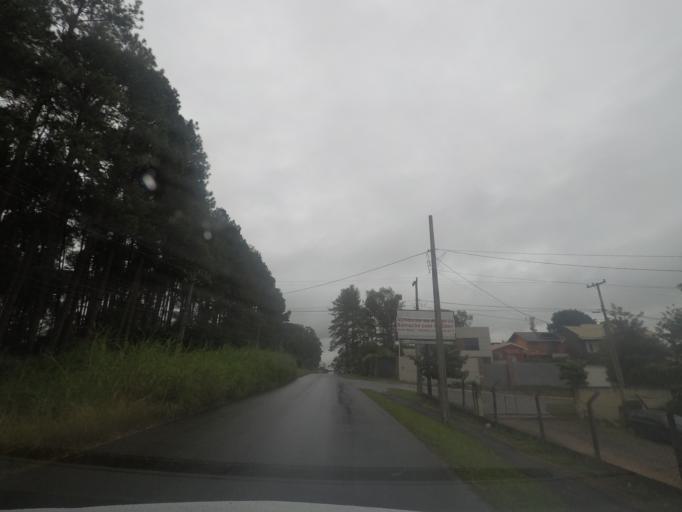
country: BR
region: Parana
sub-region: Quatro Barras
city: Quatro Barras
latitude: -25.3847
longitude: -49.1362
